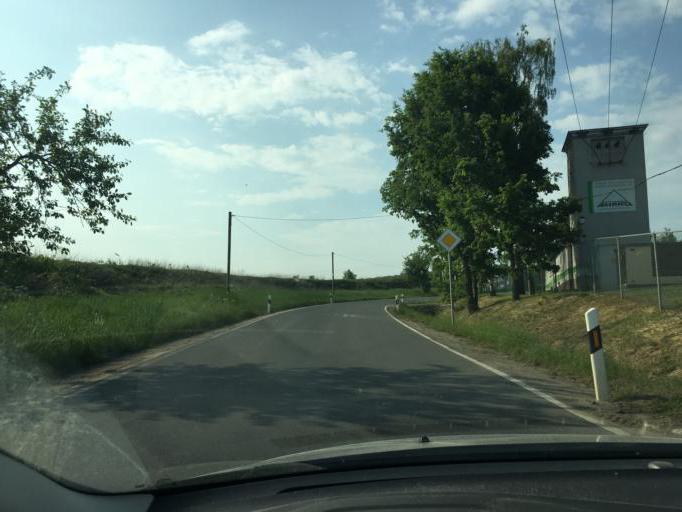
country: DE
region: Saxony
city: Rochlitz
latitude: 51.0606
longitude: 12.8046
